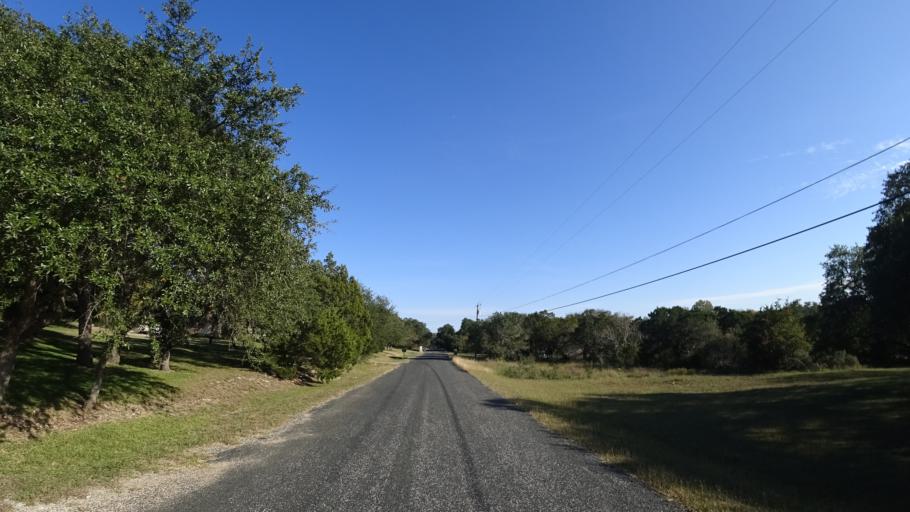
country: US
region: Texas
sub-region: Travis County
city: Barton Creek
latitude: 30.2454
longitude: -97.9119
